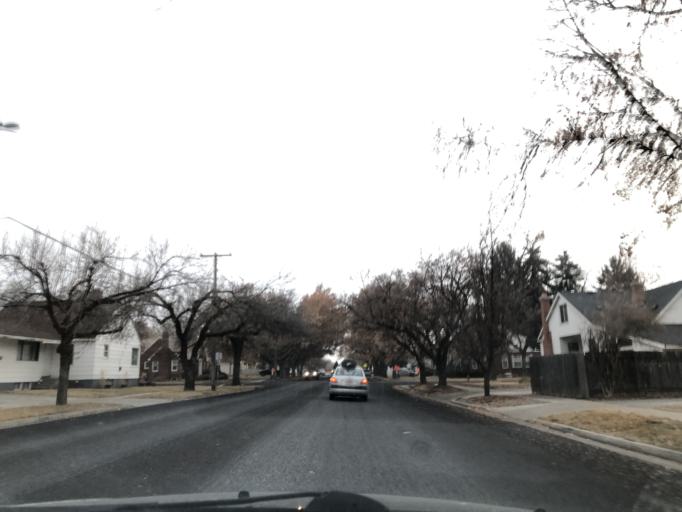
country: US
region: Utah
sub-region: Cache County
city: Logan
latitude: 41.7435
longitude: -111.8295
